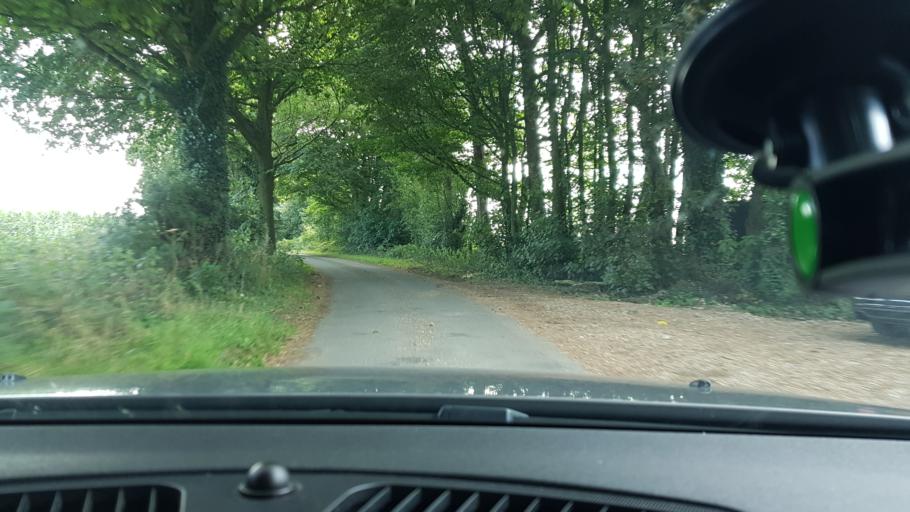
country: GB
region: England
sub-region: Wiltshire
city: Chilton Foliat
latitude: 51.4631
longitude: -1.5450
